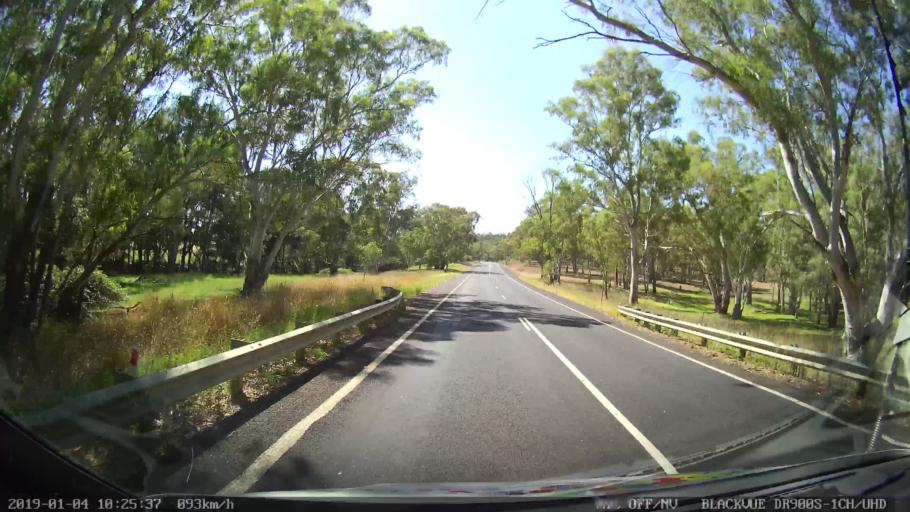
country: AU
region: New South Wales
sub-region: Cabonne
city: Canowindra
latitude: -33.3706
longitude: 148.5722
